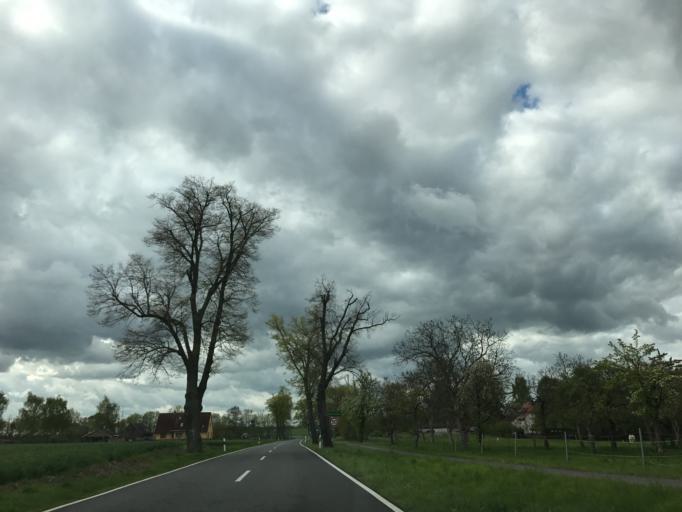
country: DE
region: Brandenburg
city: Pawesin
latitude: 52.5751
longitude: 12.7651
